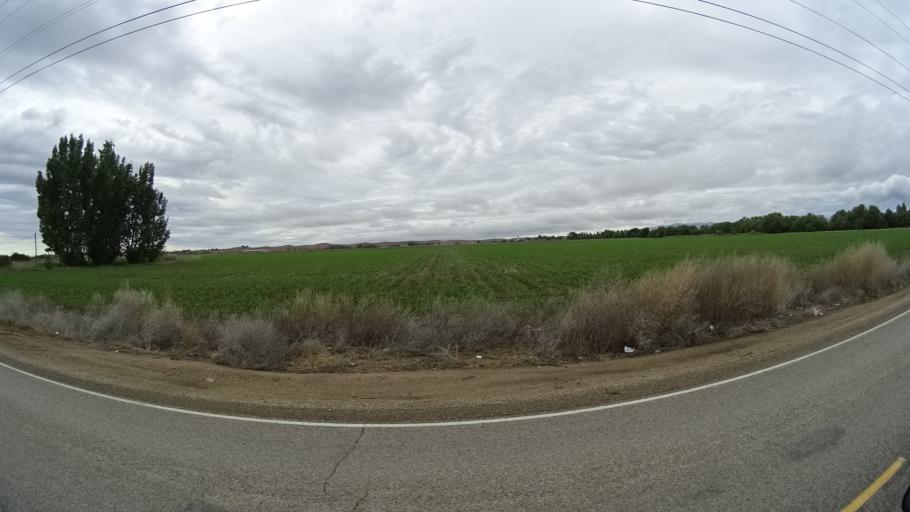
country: US
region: Idaho
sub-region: Ada County
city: Star
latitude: 43.7076
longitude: -116.4381
